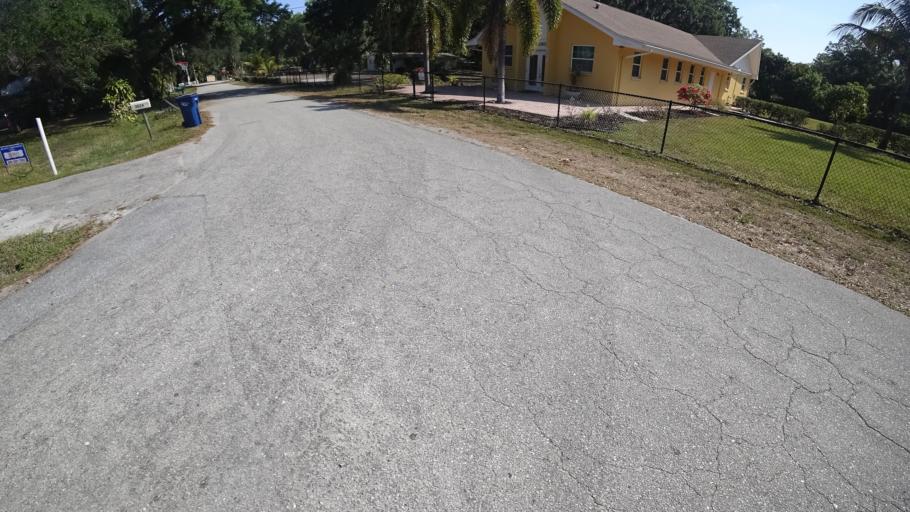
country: US
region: Florida
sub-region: Manatee County
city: Samoset
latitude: 27.4723
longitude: -82.5374
